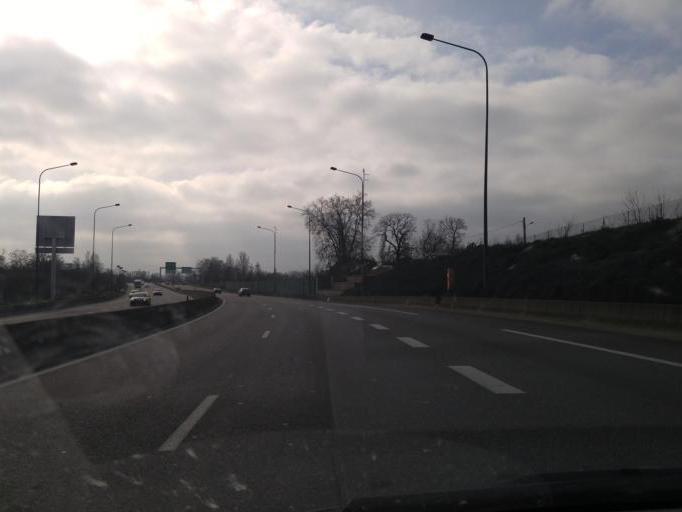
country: FR
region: Midi-Pyrenees
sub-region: Departement de la Haute-Garonne
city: Blagnac
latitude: 43.6145
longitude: 1.3875
